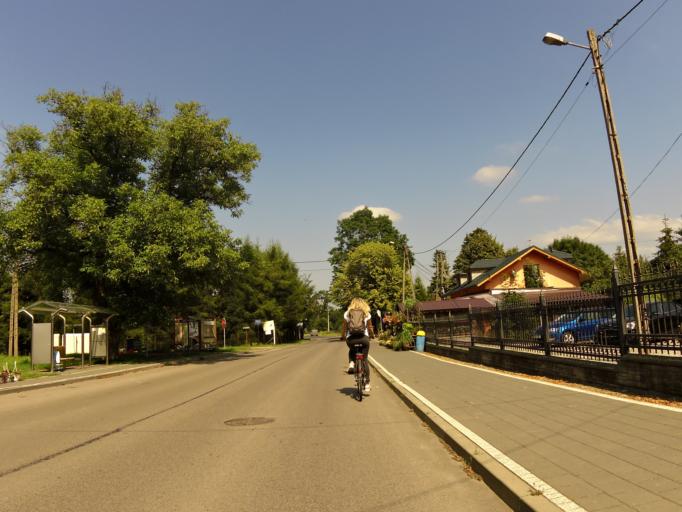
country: PL
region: Silesian Voivodeship
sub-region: Powiat zywiecki
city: Ciecina
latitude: 49.6177
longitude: 19.1388
